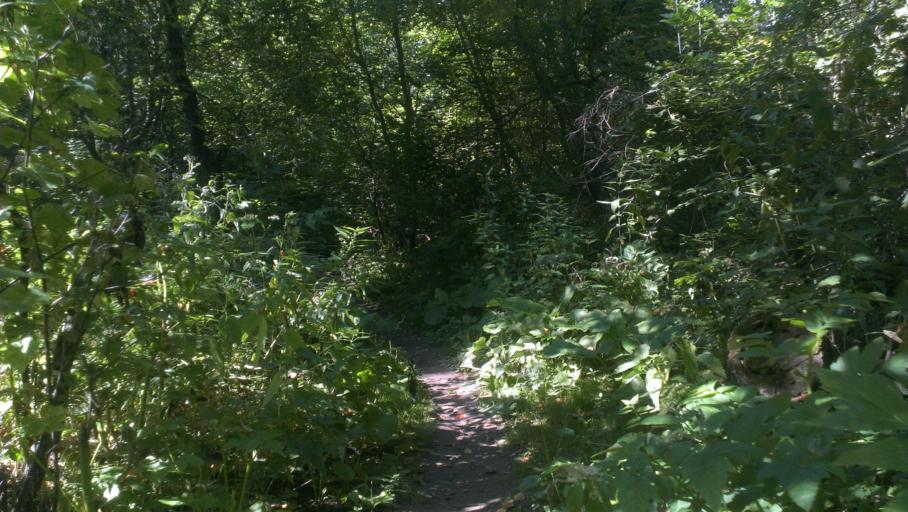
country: RU
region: Altai Krai
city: Nauchnyy Gorodok
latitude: 53.4258
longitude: 83.5047
